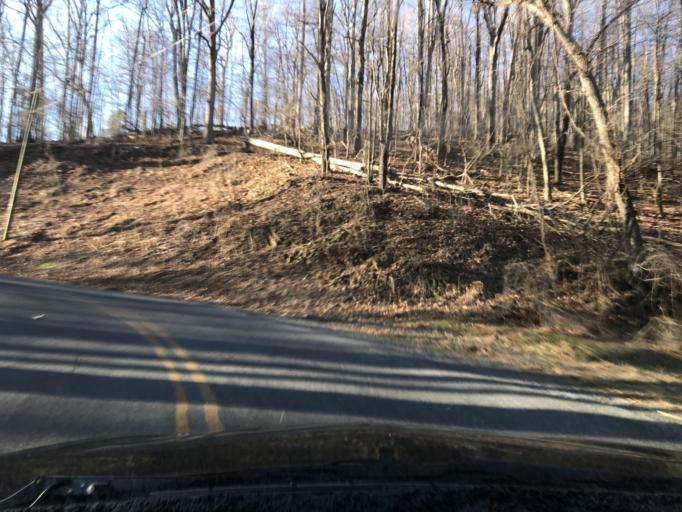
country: US
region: Virginia
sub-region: Botetourt County
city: Buchanan
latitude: 37.4762
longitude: -79.6568
